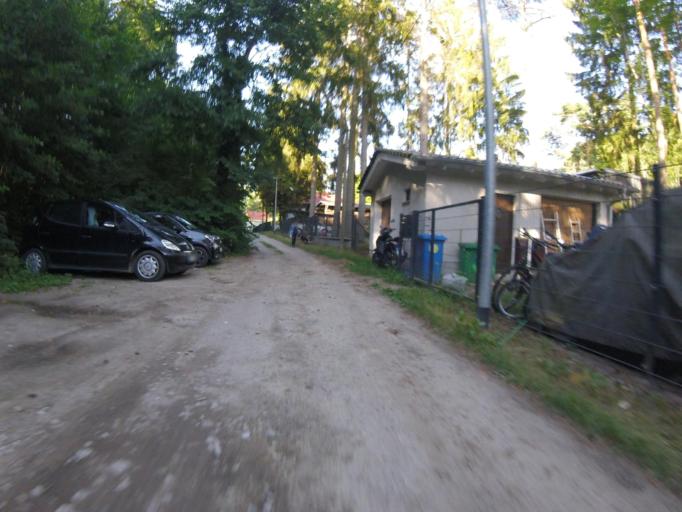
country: DE
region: Brandenburg
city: Wildau
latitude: 52.3223
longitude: 13.7147
